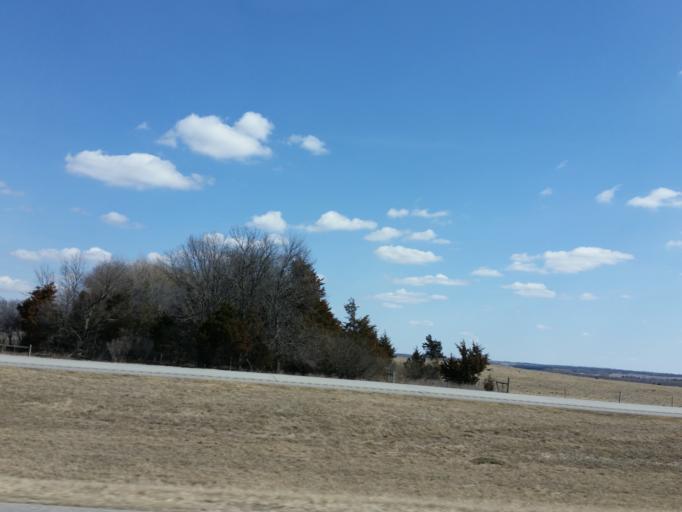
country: US
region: South Dakota
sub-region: Codington County
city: Watertown
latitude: 44.9220
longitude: -97.0563
